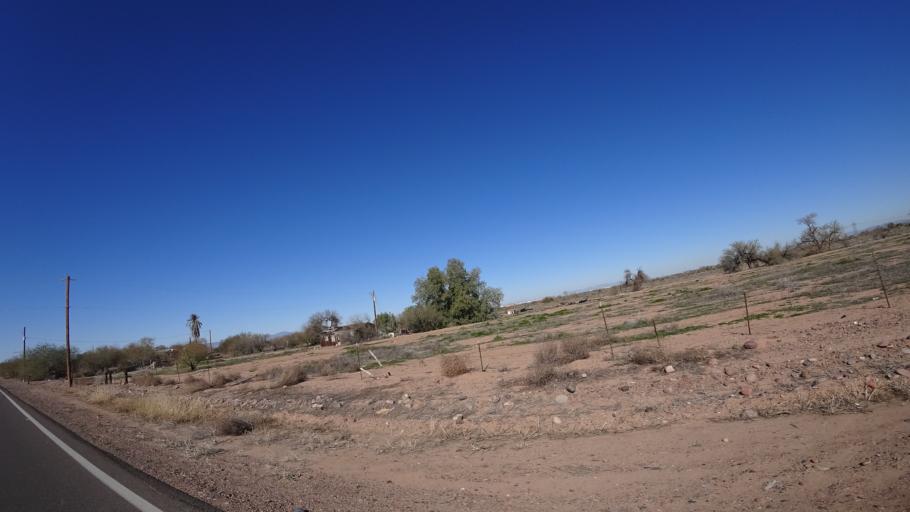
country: US
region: Arizona
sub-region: Maricopa County
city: Laveen
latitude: 33.3773
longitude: -112.2404
